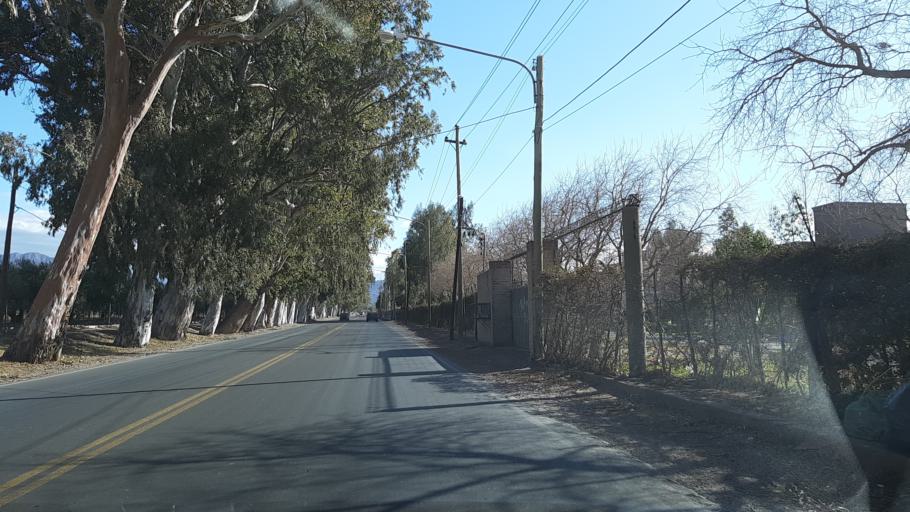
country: AR
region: San Juan
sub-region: Departamento de Rivadavia
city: Rivadavia
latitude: -31.5389
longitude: -68.6043
